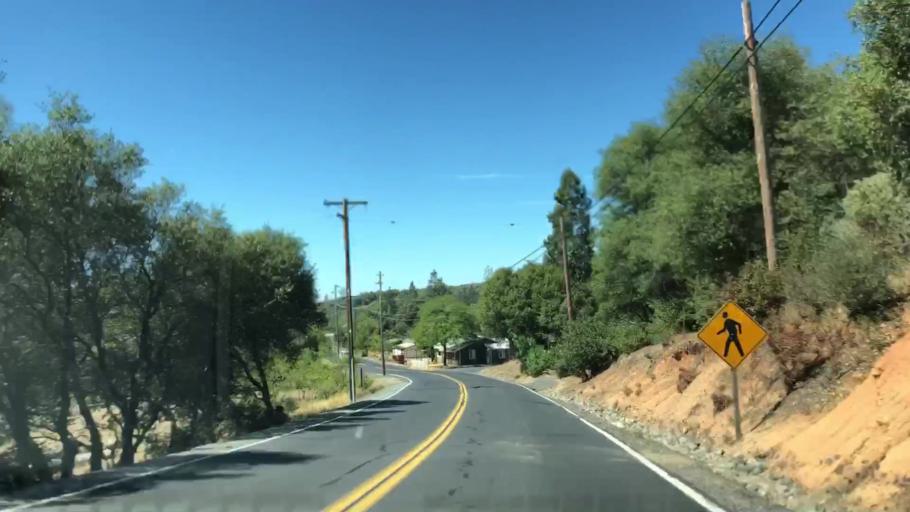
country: US
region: California
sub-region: Tuolumne County
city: Tuolumne City
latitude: 37.8252
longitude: -120.2552
